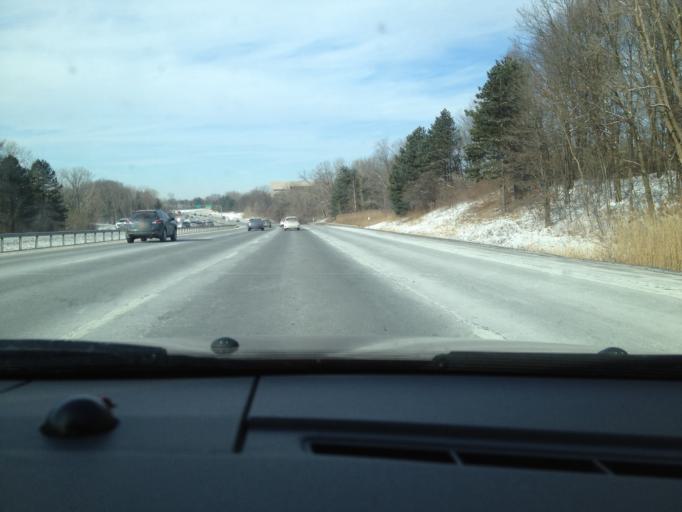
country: US
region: New York
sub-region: Albany County
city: West Albany
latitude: 42.6769
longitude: -73.7629
